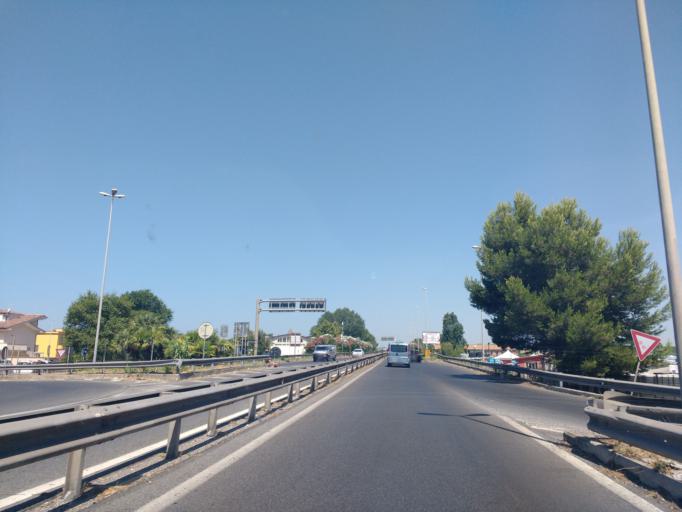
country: IT
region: Latium
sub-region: Citta metropolitana di Roma Capitale
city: Fiumicino-Isola Sacra
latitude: 41.7695
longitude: 12.2595
